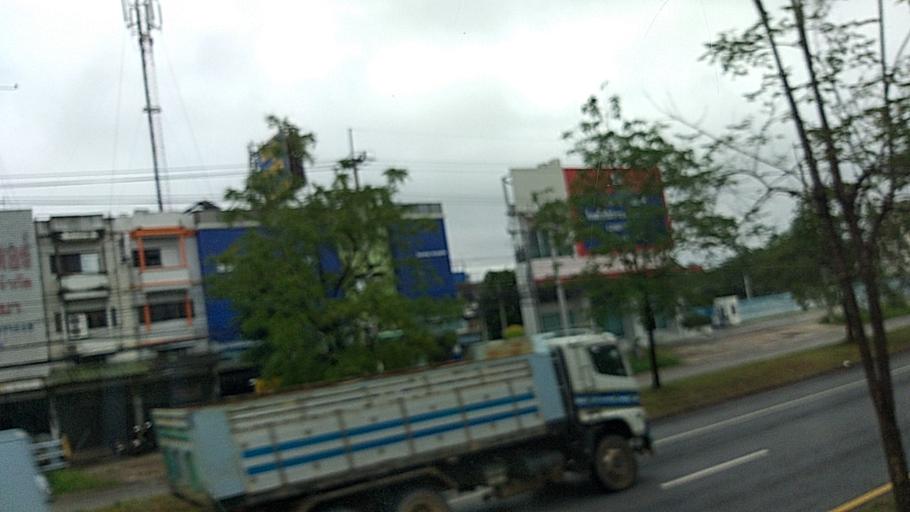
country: TH
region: Nakhon Ratchasima
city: Nakhon Ratchasima
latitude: 15.0185
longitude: 102.1318
